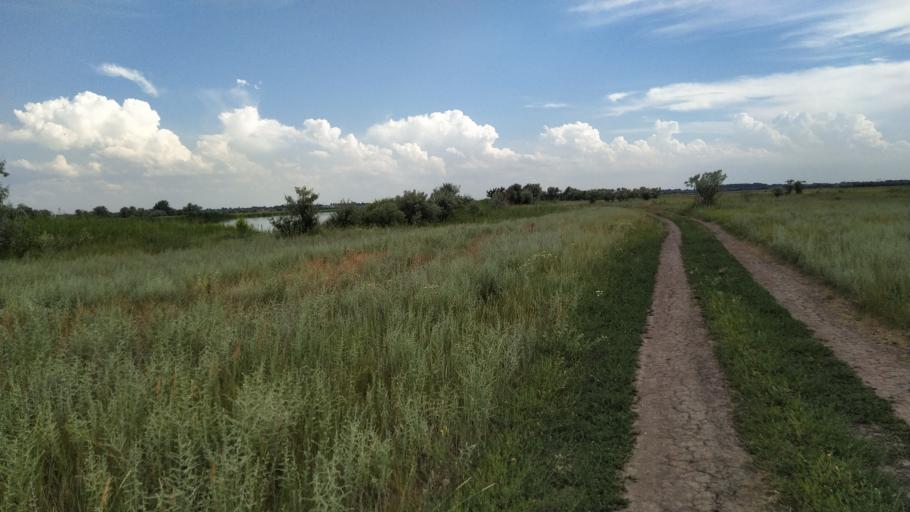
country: RU
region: Rostov
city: Kuleshovka
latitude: 47.1333
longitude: 39.6302
